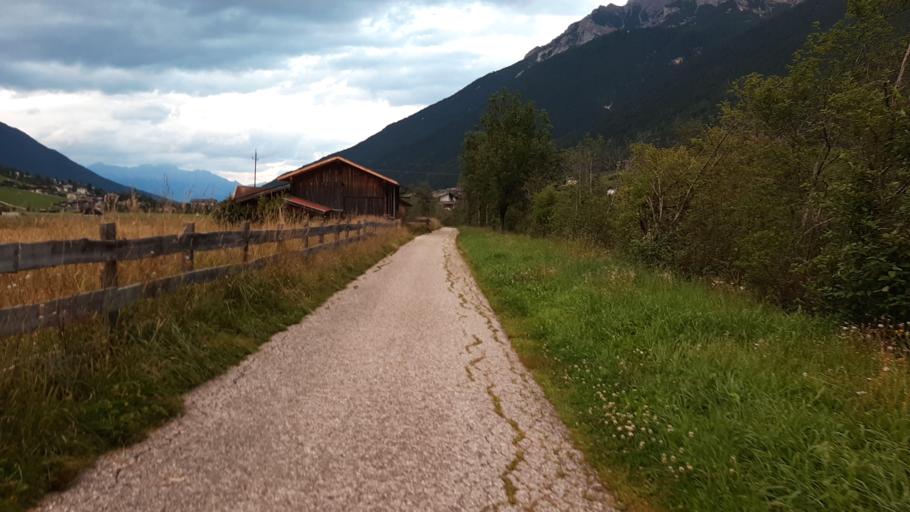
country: AT
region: Tyrol
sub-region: Politischer Bezirk Innsbruck Land
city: Neustift im Stubaital
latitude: 47.1138
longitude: 11.3187
